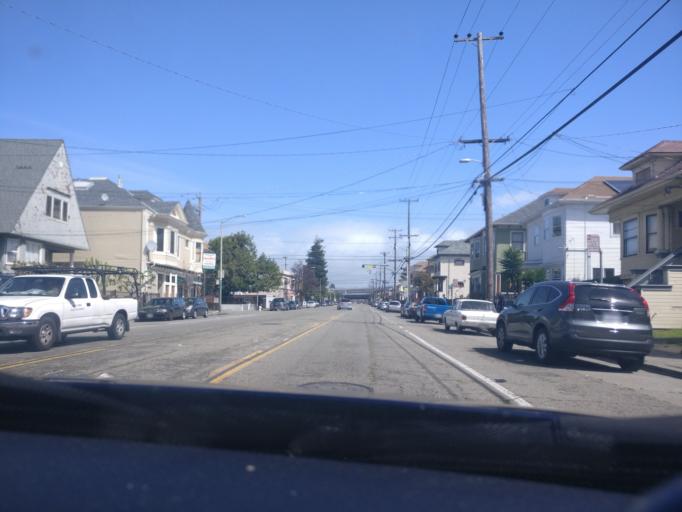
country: US
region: California
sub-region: Alameda County
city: Emeryville
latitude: 37.8214
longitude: -122.2732
